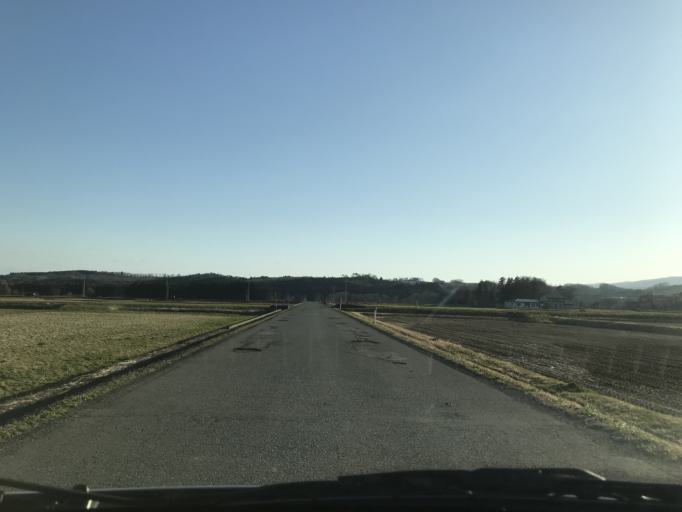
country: JP
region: Iwate
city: Kitakami
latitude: 39.2127
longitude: 141.0369
